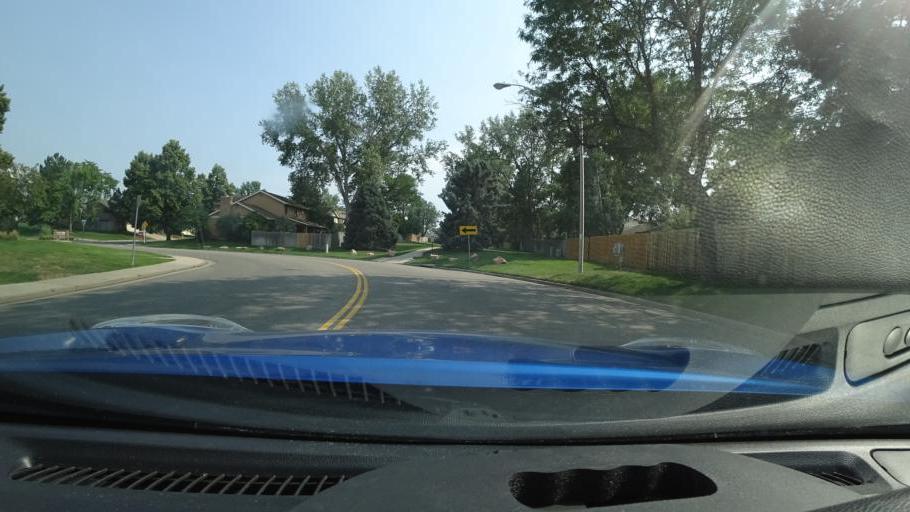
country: US
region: Colorado
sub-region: Adams County
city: Aurora
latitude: 39.6666
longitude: -104.8392
